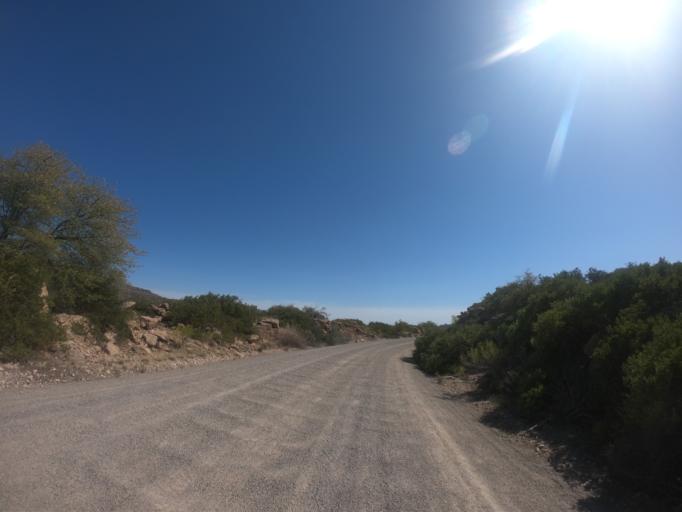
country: US
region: Arizona
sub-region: Pinal County
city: Superior
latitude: 33.3190
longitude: -111.0439
